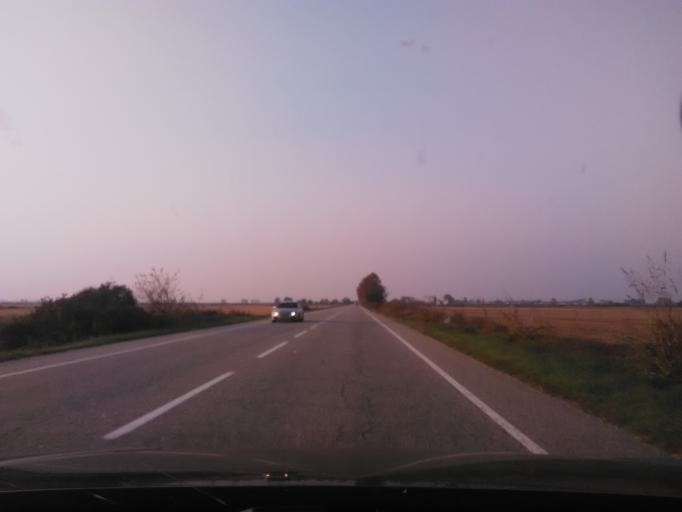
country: IT
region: Piedmont
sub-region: Provincia di Vercelli
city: Stroppiana
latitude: 45.2115
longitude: 8.4586
